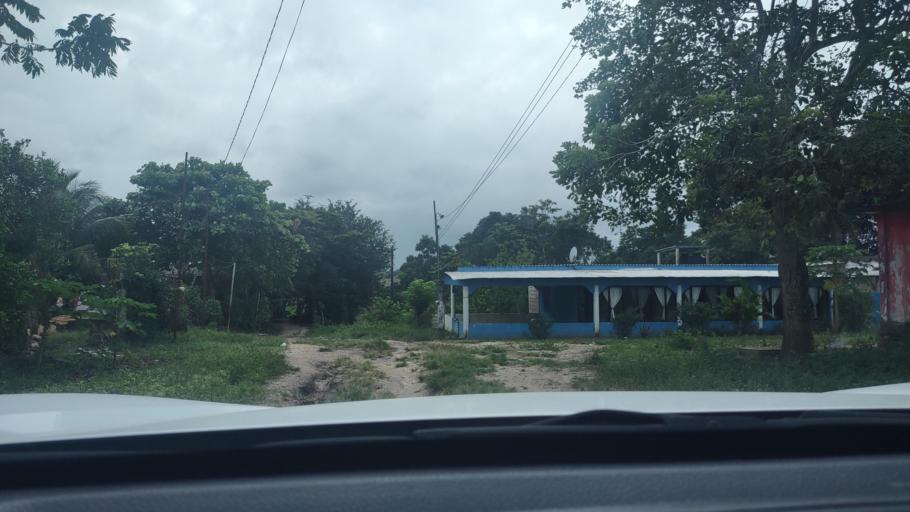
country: MX
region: Veracruz
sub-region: Moloacan
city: Cuichapa
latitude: 17.8985
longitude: -94.2984
